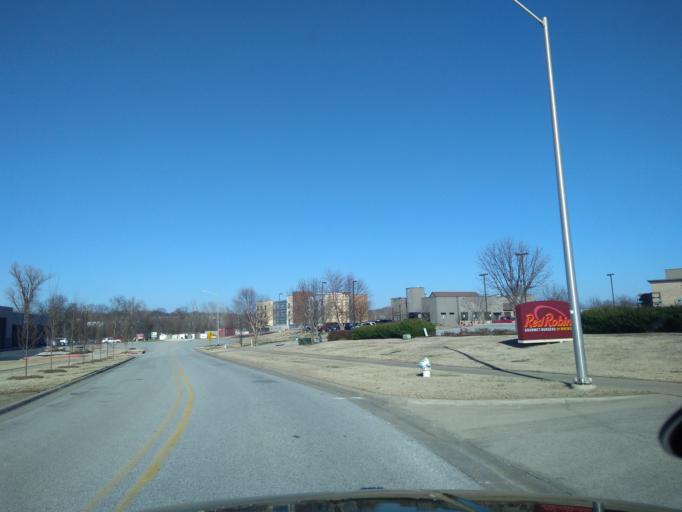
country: US
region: Arkansas
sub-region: Washington County
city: Johnson
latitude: 36.1178
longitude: -94.1486
